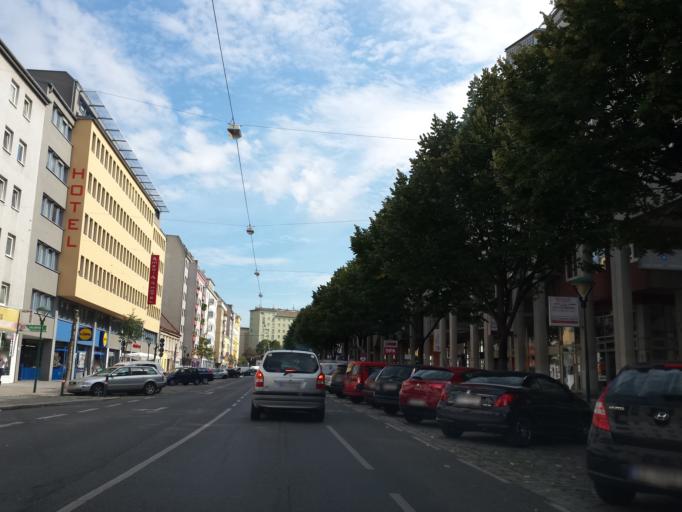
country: AT
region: Vienna
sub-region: Wien Stadt
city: Vienna
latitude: 48.1927
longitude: 16.3988
